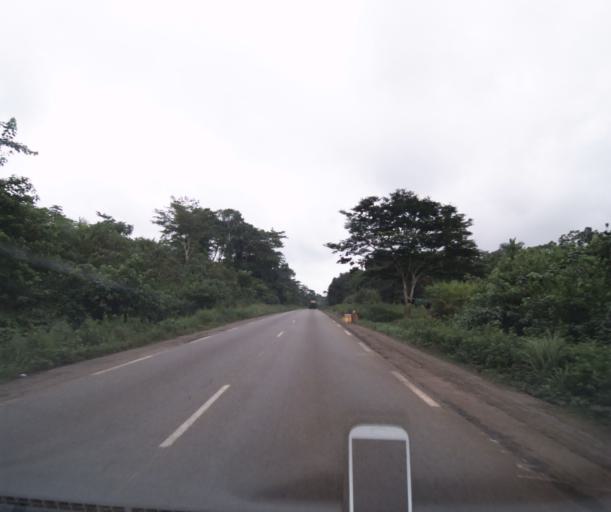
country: CM
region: Littoral
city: Edea
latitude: 3.8131
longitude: 10.3131
